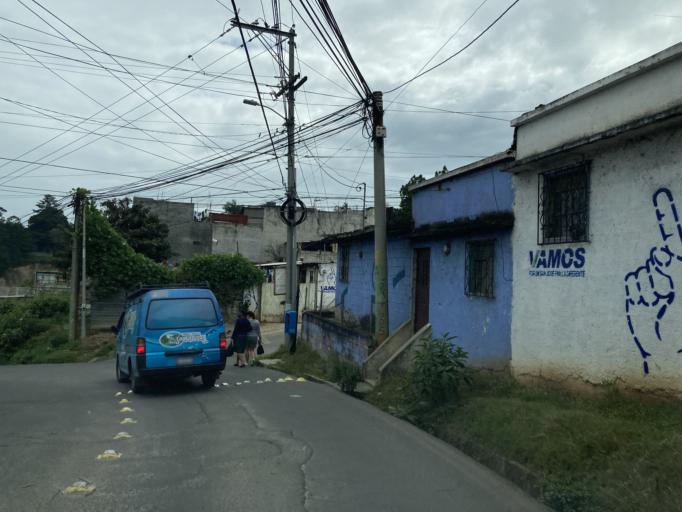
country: GT
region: Guatemala
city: San Jose Pinula
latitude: 14.5387
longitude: -90.4072
